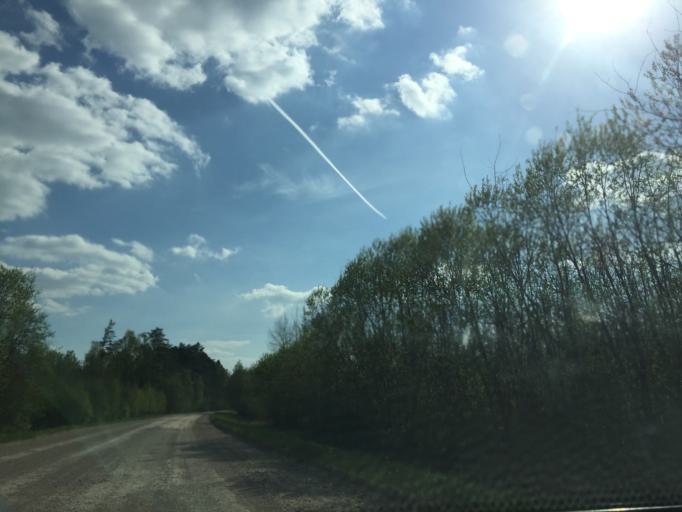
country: LV
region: Vecumnieki
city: Vecumnieki
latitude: 56.5139
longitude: 24.4085
